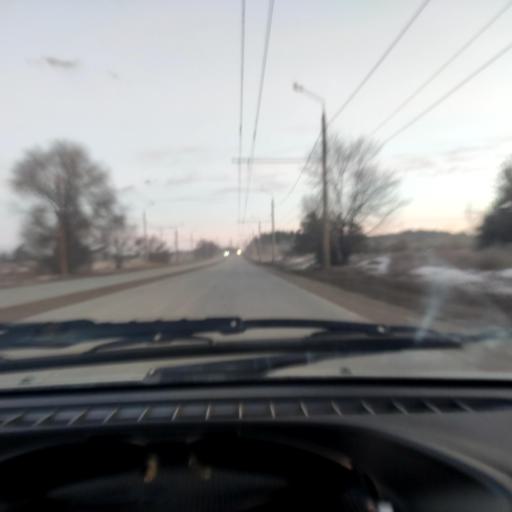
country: RU
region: Samara
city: Zhigulevsk
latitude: 53.5026
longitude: 49.5148
